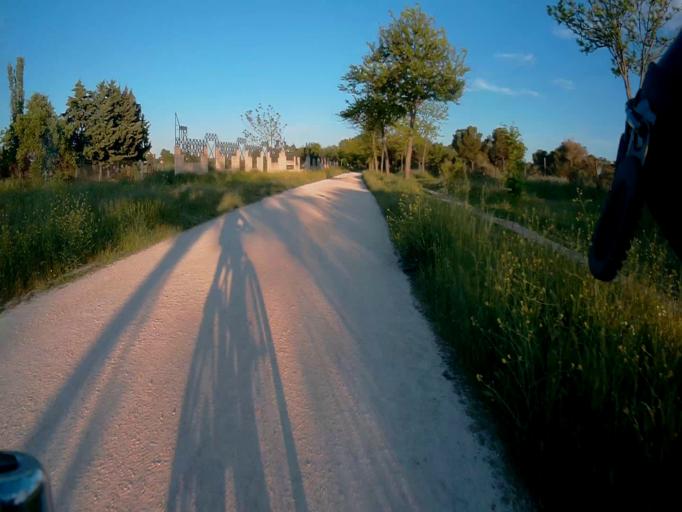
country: ES
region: Madrid
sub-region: Provincia de Madrid
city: Alcorcon
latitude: 40.3284
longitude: -3.7974
